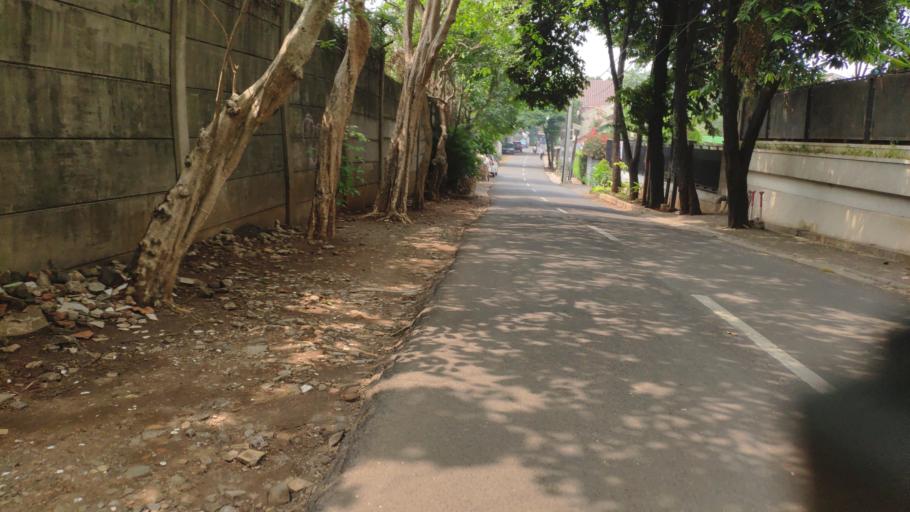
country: ID
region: West Java
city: Depok
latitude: -6.3247
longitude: 106.8226
